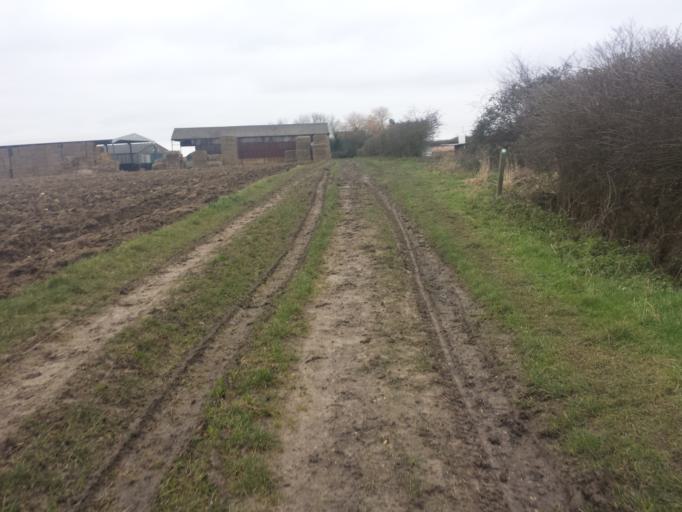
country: GB
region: England
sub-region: Essex
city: Little Clacton
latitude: 51.8687
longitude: 1.1614
